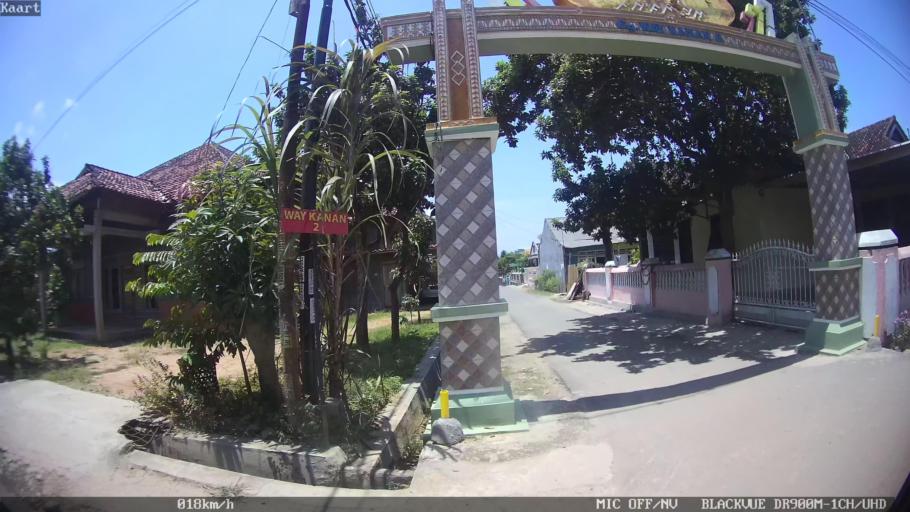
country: ID
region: Lampung
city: Kedaton
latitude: -5.3732
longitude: 105.2803
